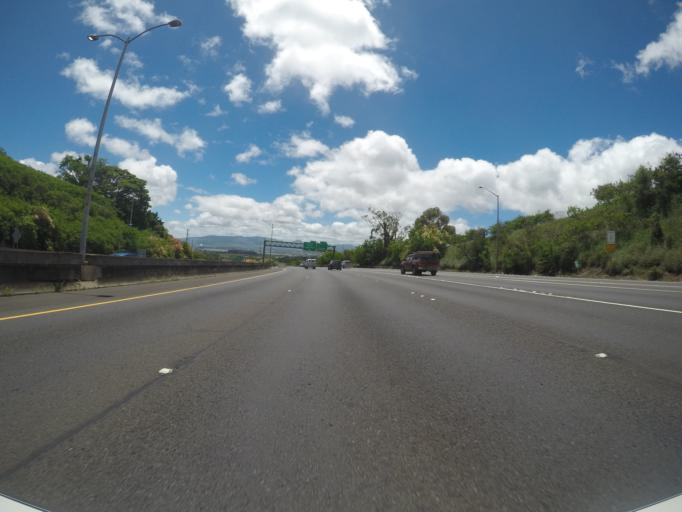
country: US
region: Hawaii
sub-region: Honolulu County
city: Halawa Heights
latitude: 21.3681
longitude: -157.9061
